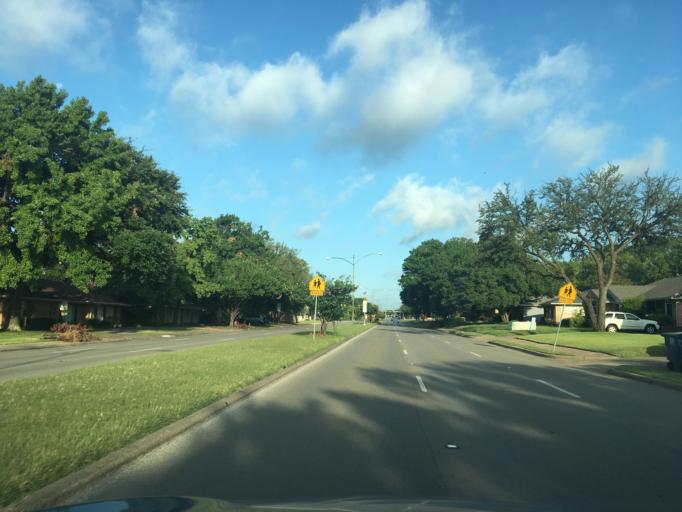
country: US
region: Texas
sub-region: Dallas County
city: Highland Park
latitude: 32.8510
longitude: -96.7555
